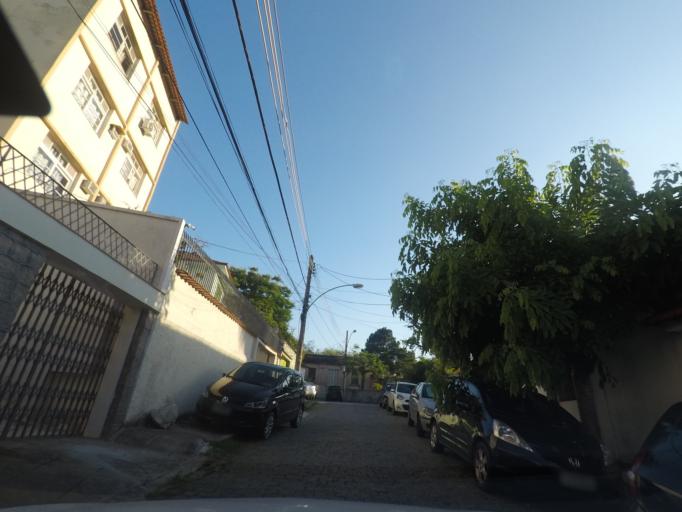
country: BR
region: Rio de Janeiro
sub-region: Rio De Janeiro
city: Rio de Janeiro
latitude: -22.9410
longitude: -43.1933
